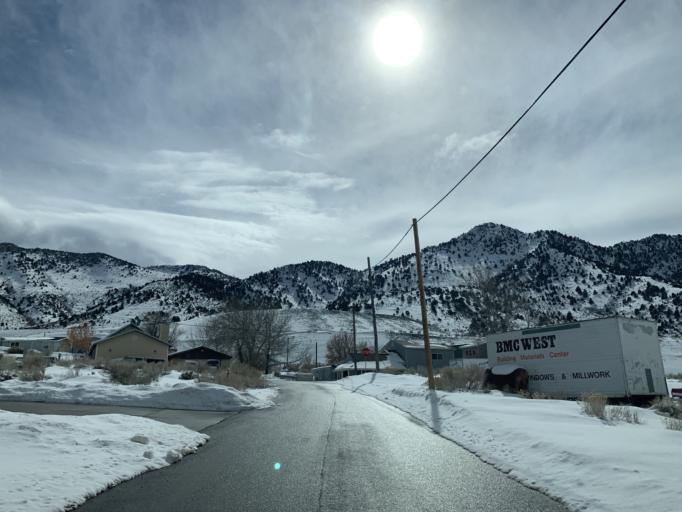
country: US
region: Utah
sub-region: Utah County
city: Genola
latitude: 39.9524
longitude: -112.1213
